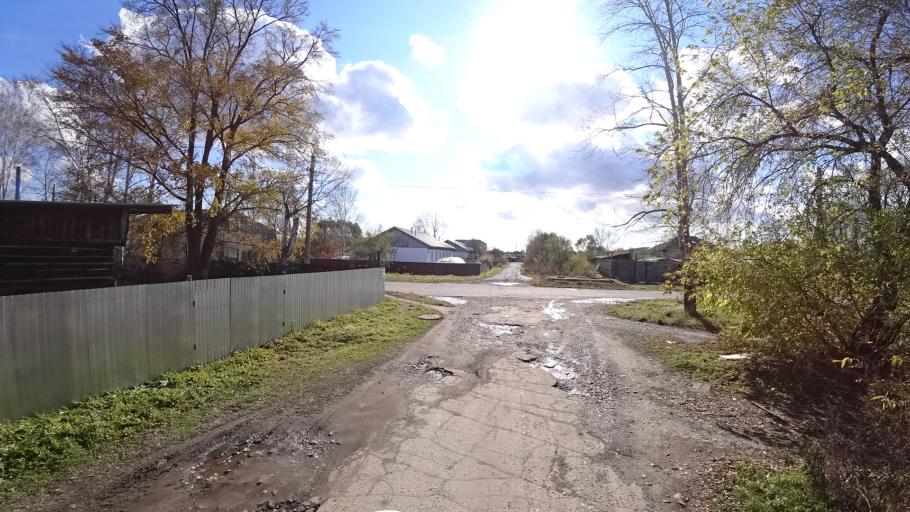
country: RU
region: Khabarovsk Krai
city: Amursk
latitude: 50.1001
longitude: 136.5005
